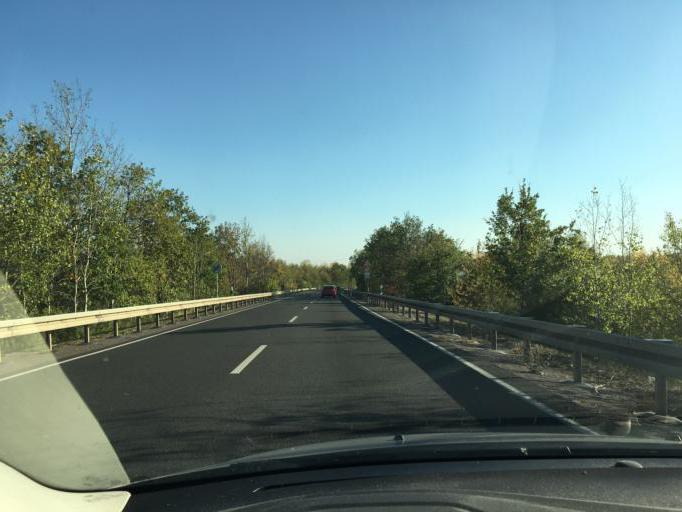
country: DE
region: Saxony-Anhalt
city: Roitzsch
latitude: 51.5824
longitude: 12.2827
